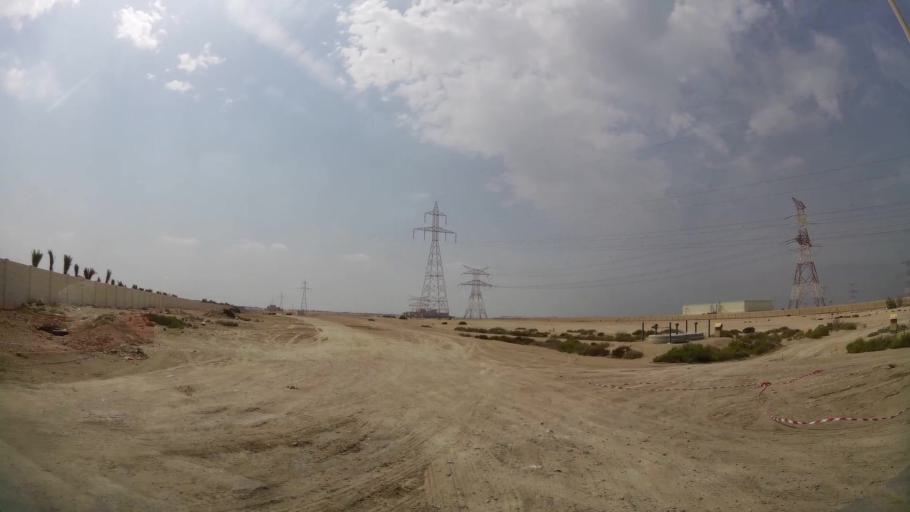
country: AE
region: Abu Dhabi
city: Abu Dhabi
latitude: 24.5221
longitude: 54.6494
